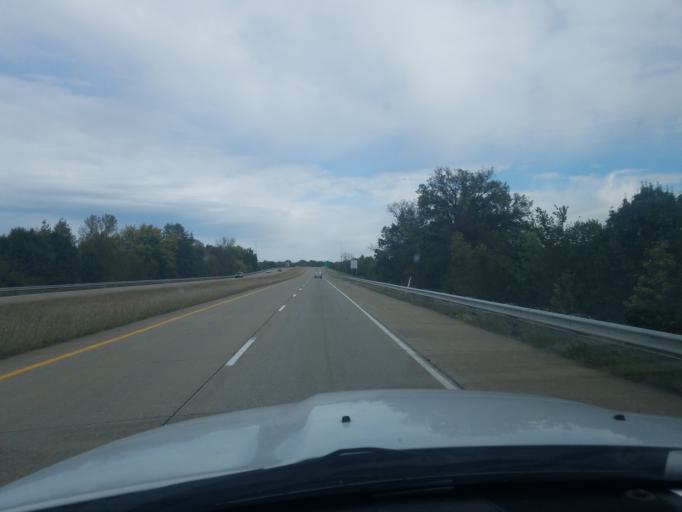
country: US
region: Indiana
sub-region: Warrick County
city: Newburgh
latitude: 37.9449
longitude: -87.4764
